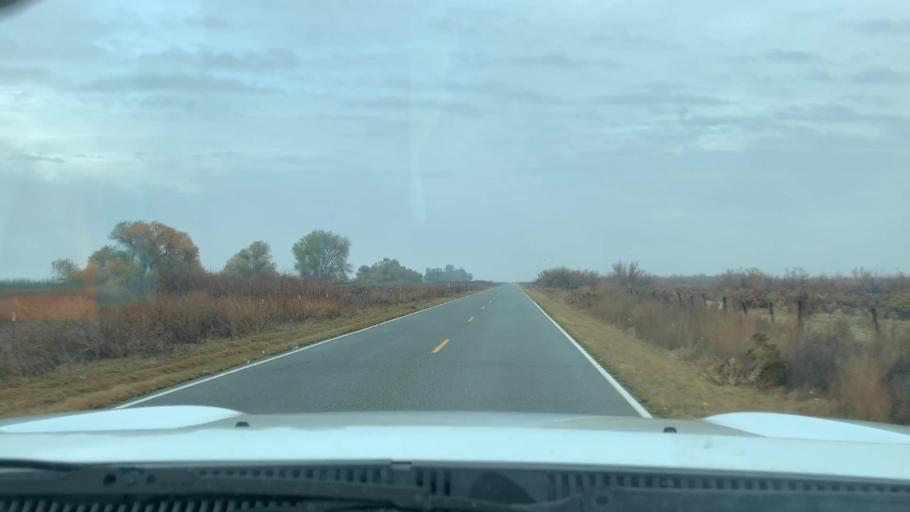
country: US
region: California
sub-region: Kern County
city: Lost Hills
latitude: 35.7263
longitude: -119.5794
